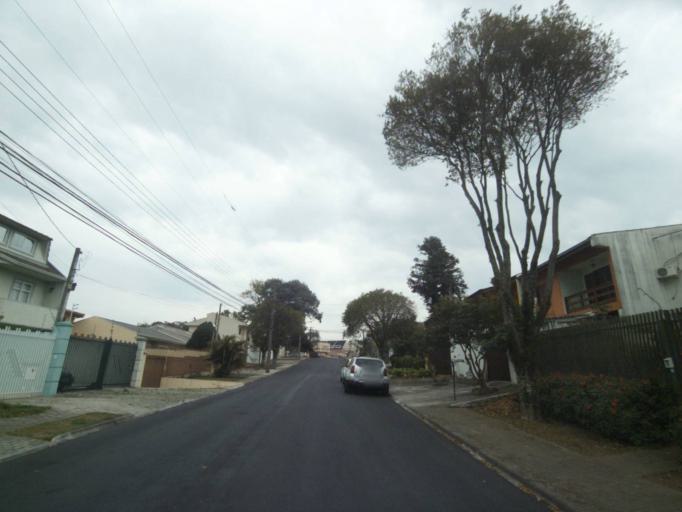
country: BR
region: Parana
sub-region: Pinhais
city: Pinhais
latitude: -25.4731
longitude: -49.2315
